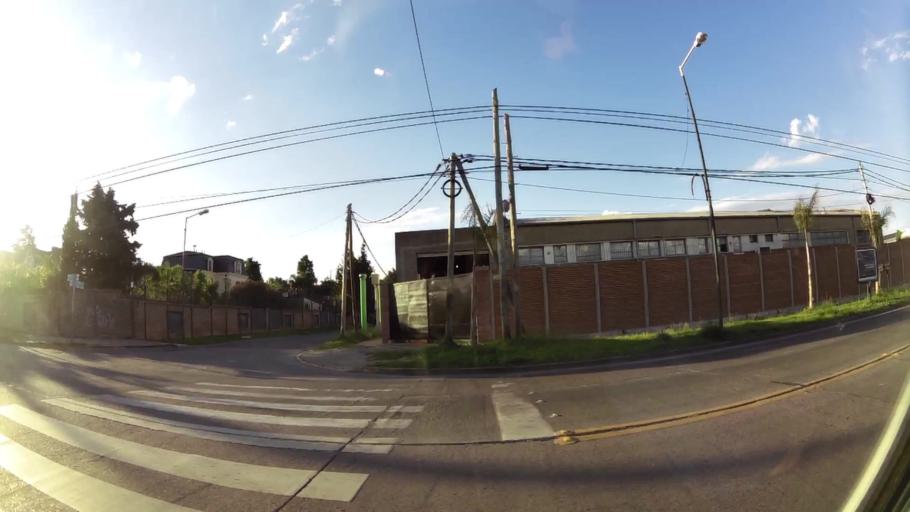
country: AR
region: Buenos Aires
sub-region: Partido de San Isidro
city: San Isidro
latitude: -34.4651
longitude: -58.5536
